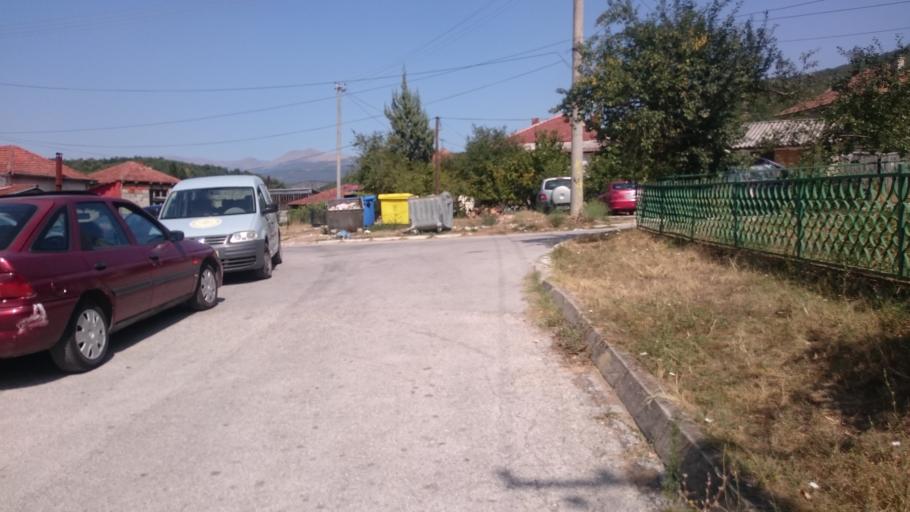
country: MK
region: Makedonski Brod
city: Makedonski Brod
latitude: 41.5064
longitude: 21.2198
